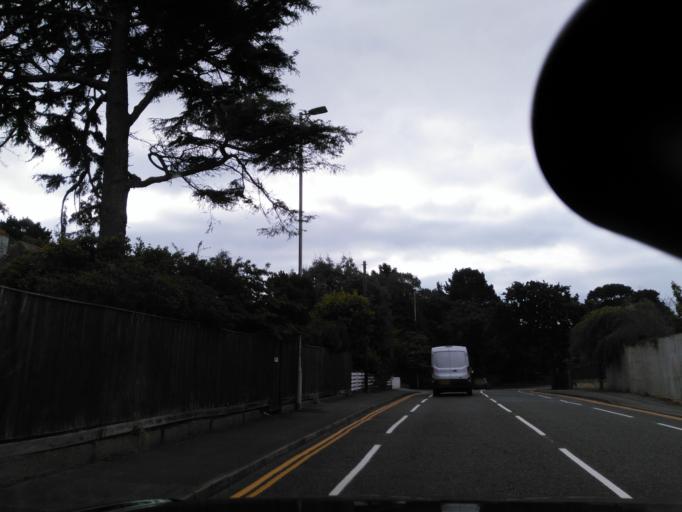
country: GB
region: England
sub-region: Dorset
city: Parkstone
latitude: 50.7076
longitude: -1.9449
